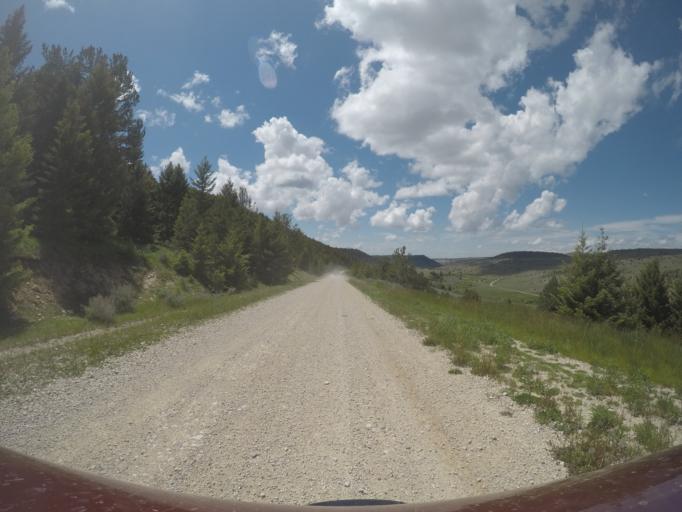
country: US
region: Wyoming
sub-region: Big Horn County
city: Lovell
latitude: 45.2084
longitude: -108.5442
